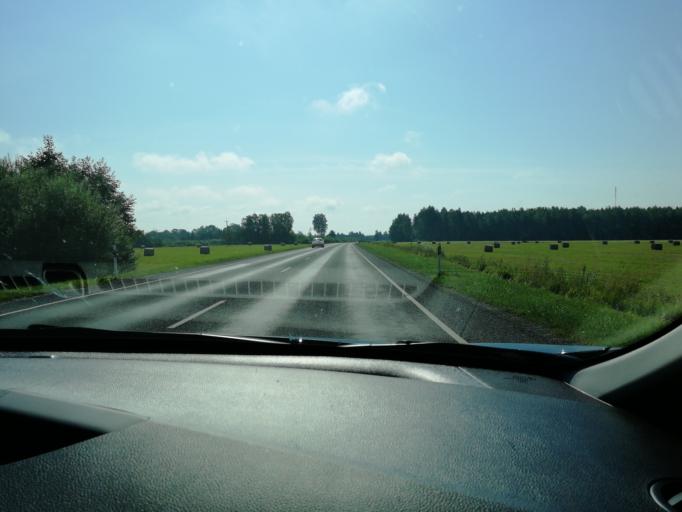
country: EE
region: Paernumaa
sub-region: Paikuse vald
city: Paikuse
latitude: 58.2008
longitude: 24.7336
